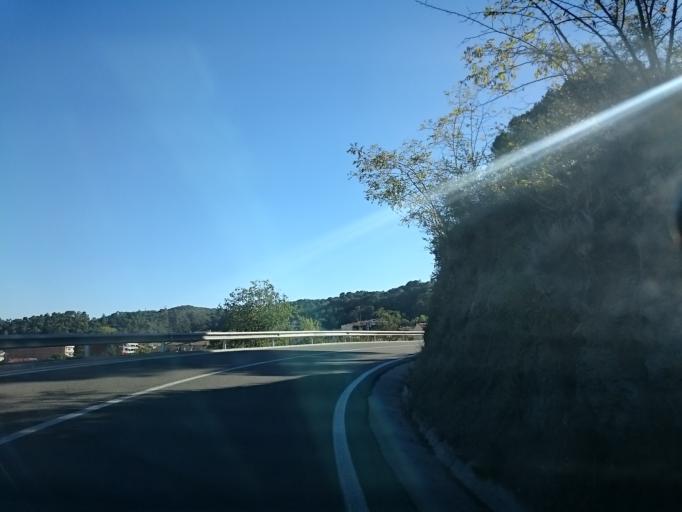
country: ES
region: Catalonia
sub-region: Provincia de Barcelona
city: Capellades
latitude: 41.5332
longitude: 1.6820
